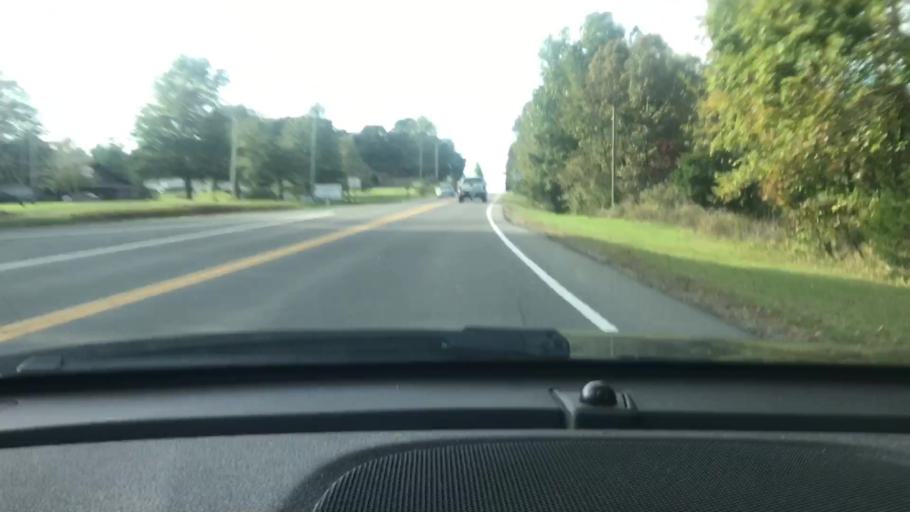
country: US
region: Tennessee
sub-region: Williamson County
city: Fairview
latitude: 35.9854
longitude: -87.1166
